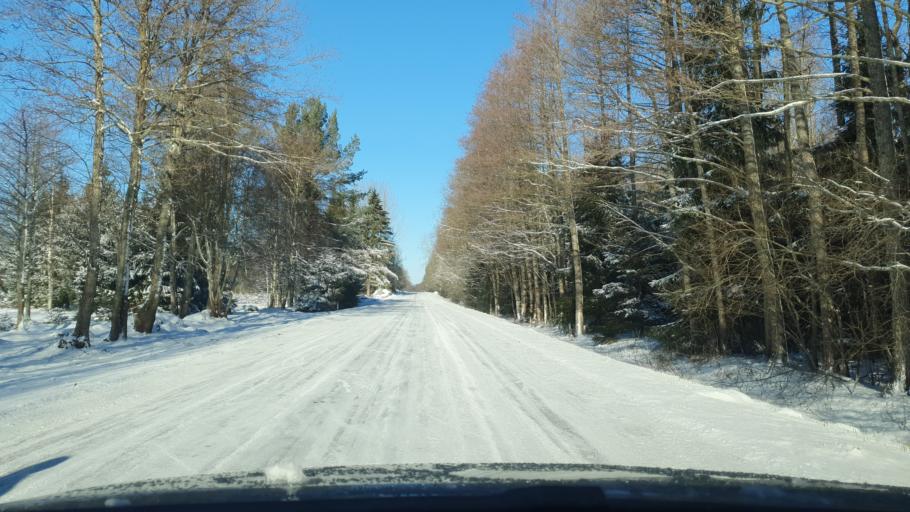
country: EE
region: Harju
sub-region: Kuusalu vald
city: Kuusalu
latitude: 59.5801
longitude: 25.5236
